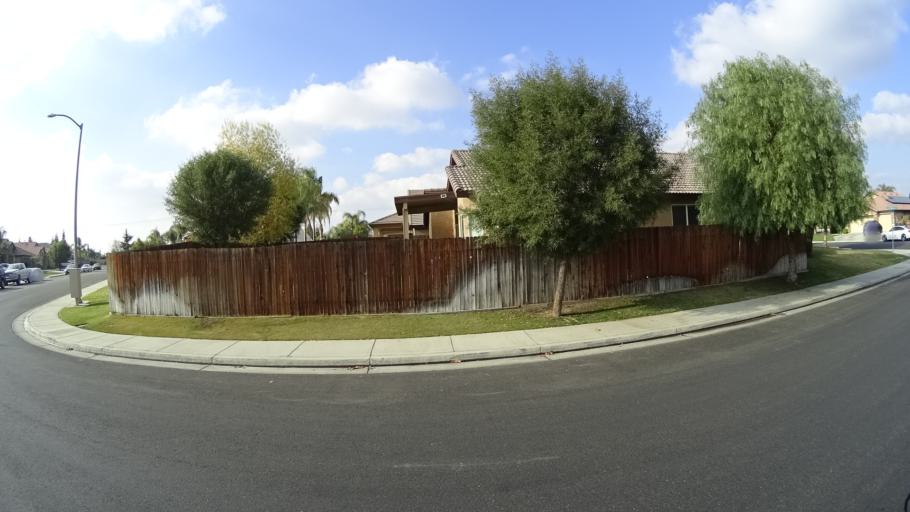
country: US
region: California
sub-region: Kern County
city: Greenacres
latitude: 35.3093
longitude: -119.1085
